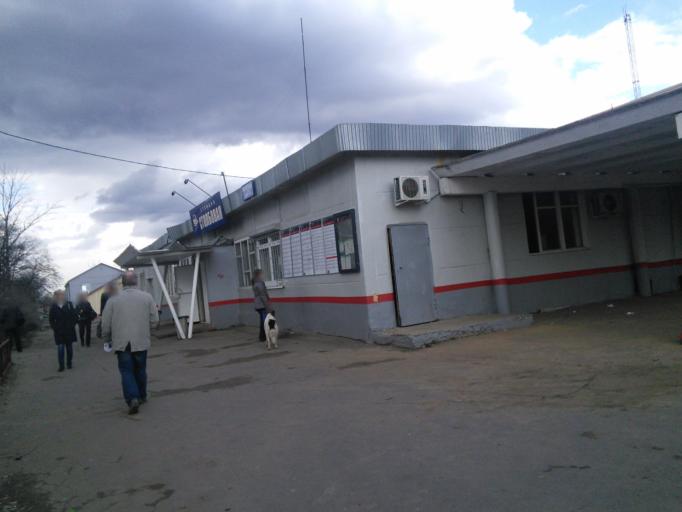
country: RU
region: Moskovskaya
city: Stolbovaya
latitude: 55.2487
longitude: 37.4942
